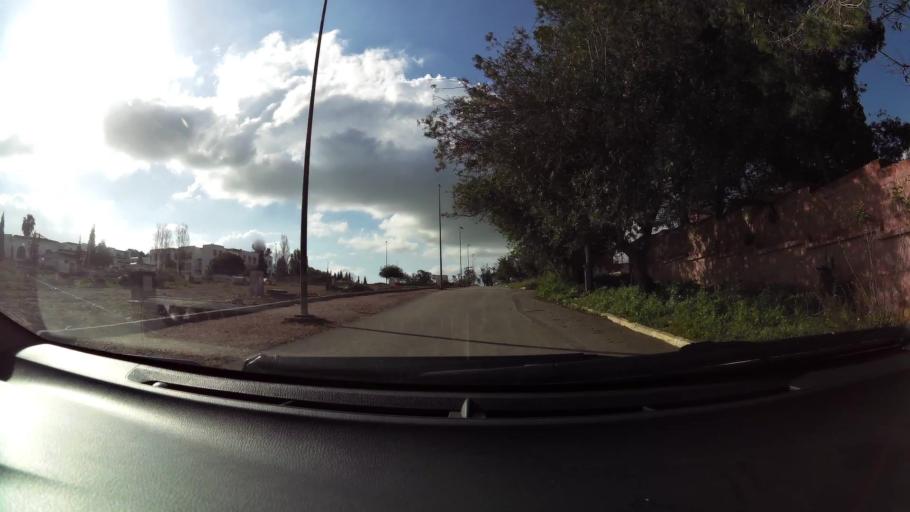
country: MA
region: Chaouia-Ouardigha
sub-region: Settat Province
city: Settat
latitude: 33.0113
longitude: -7.6349
